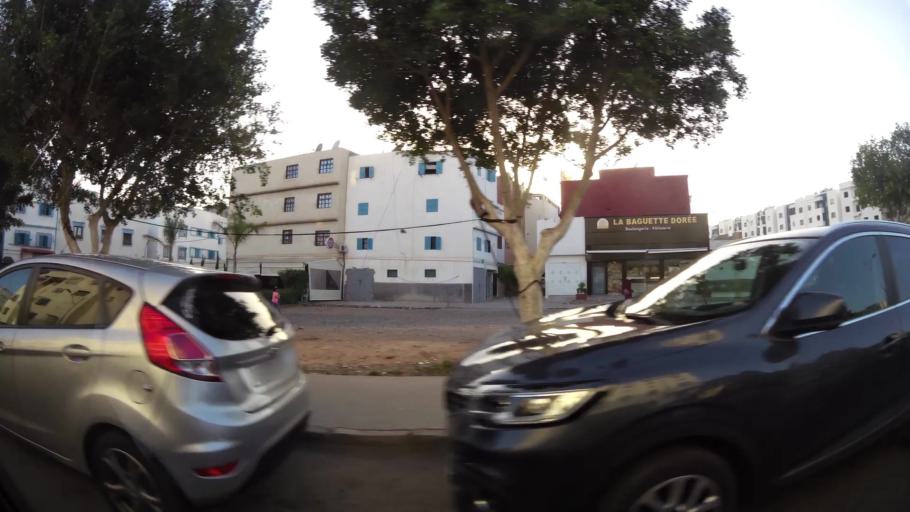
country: MA
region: Oued ed Dahab-Lagouira
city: Dakhla
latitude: 30.3907
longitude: -9.5665
